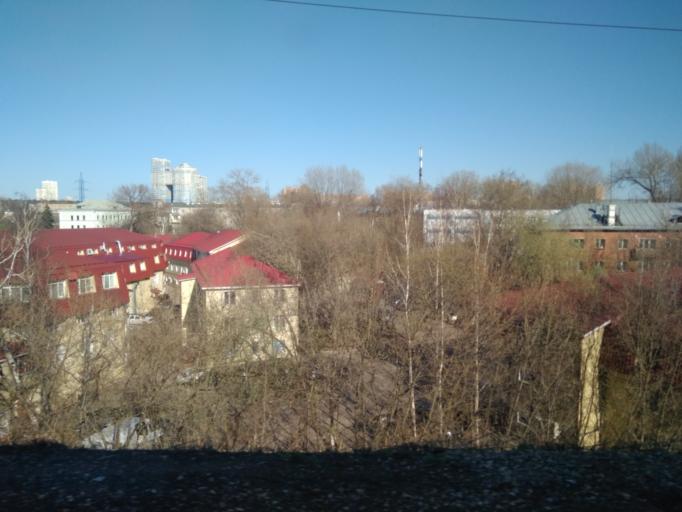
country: RU
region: Moscow
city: Pokrovskoye-Streshnevo
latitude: 55.8179
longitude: 37.4461
